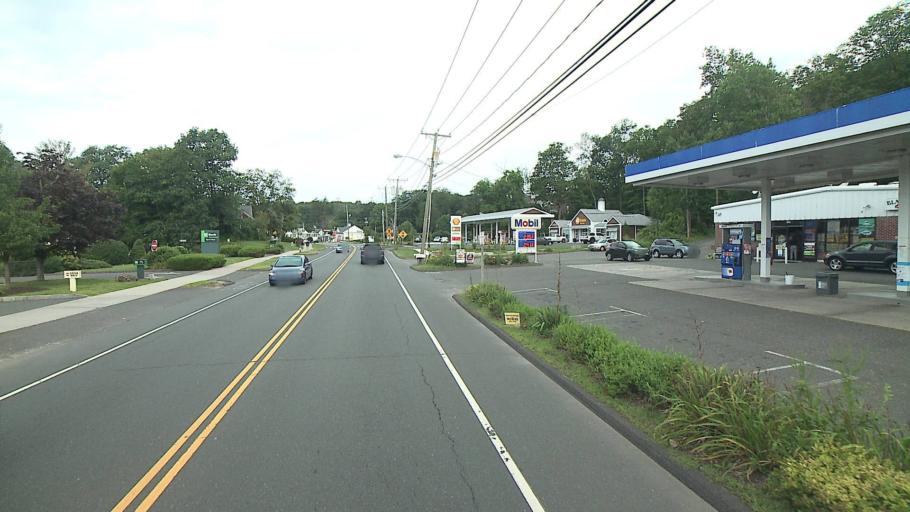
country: US
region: Connecticut
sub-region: New Haven County
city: Middlebury
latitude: 41.5378
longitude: -73.1041
